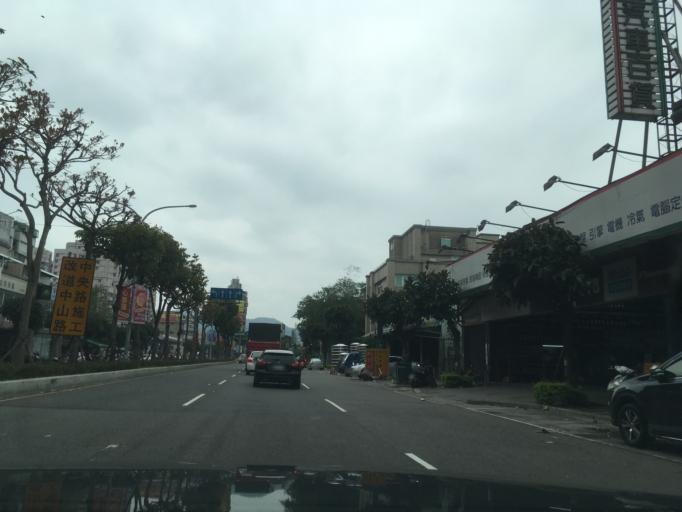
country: TW
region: Taipei
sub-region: Taipei
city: Banqiao
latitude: 24.9808
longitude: 121.4404
